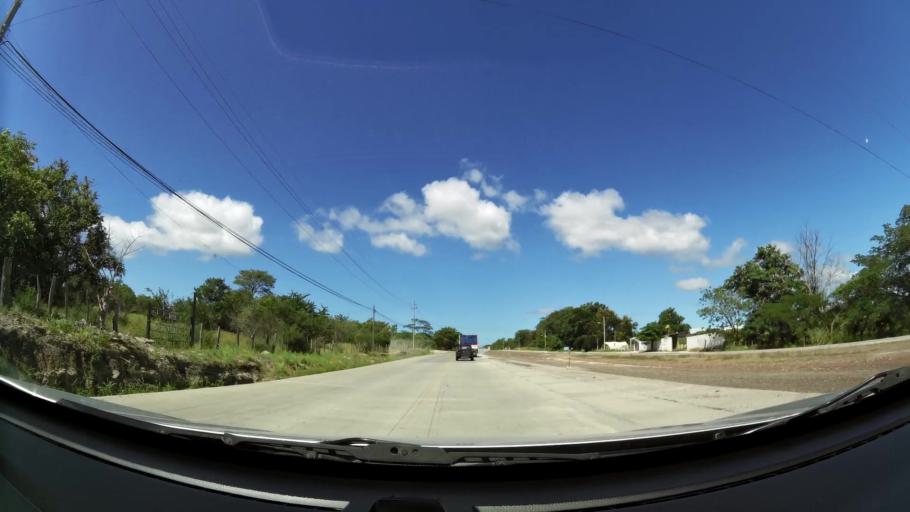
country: CR
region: Guanacaste
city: Bagaces
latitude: 10.5076
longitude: -85.2343
